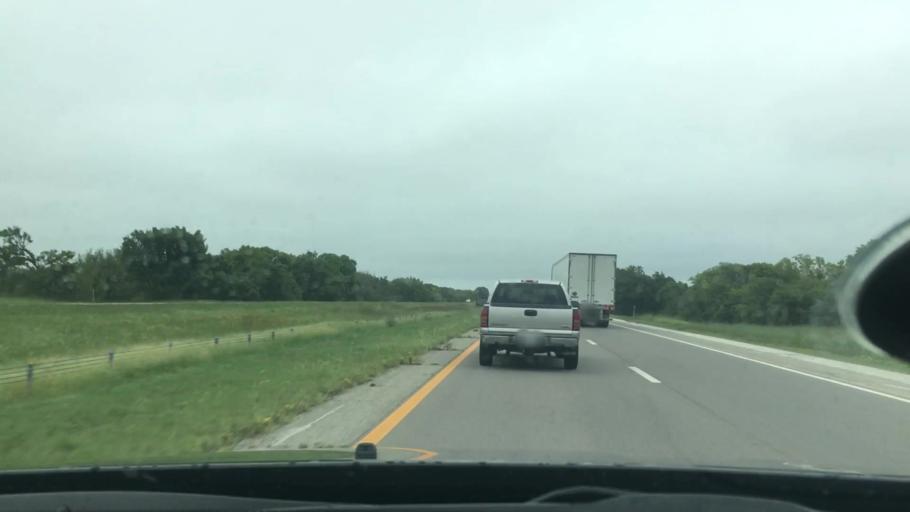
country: US
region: Oklahoma
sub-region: Okfuskee County
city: Okemah
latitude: 35.4284
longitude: -96.2407
